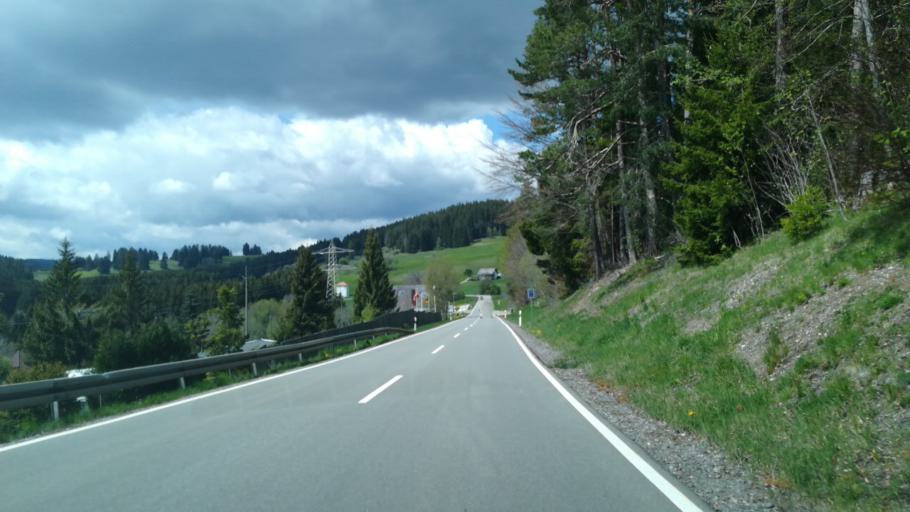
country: DE
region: Baden-Wuerttemberg
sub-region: Freiburg Region
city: Grafenhausen
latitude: 47.7946
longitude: 8.2366
